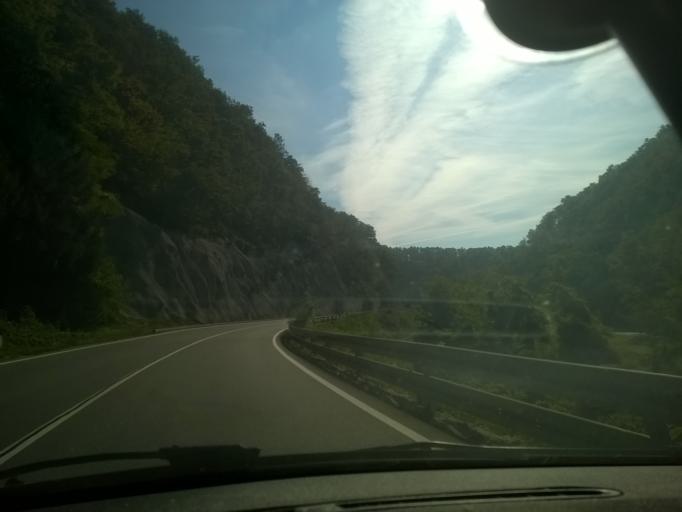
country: HR
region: Krapinsko-Zagorska
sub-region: Grad Krapina
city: Krapina
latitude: 46.1890
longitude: 15.8485
